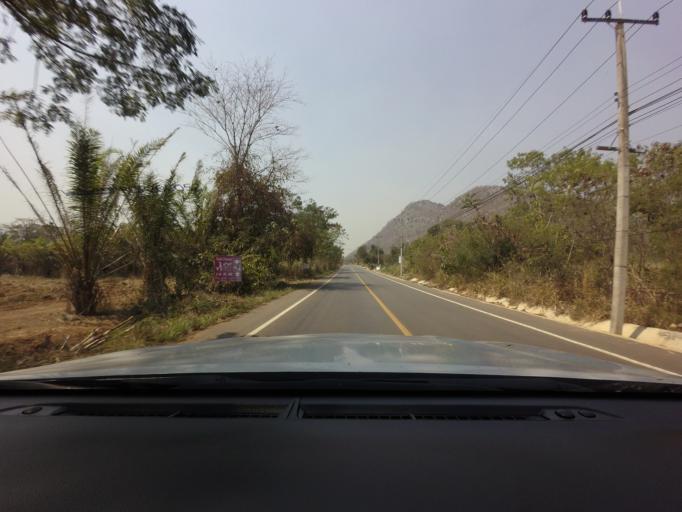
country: TH
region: Sara Buri
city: Muak Lek
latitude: 14.5522
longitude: 101.3214
